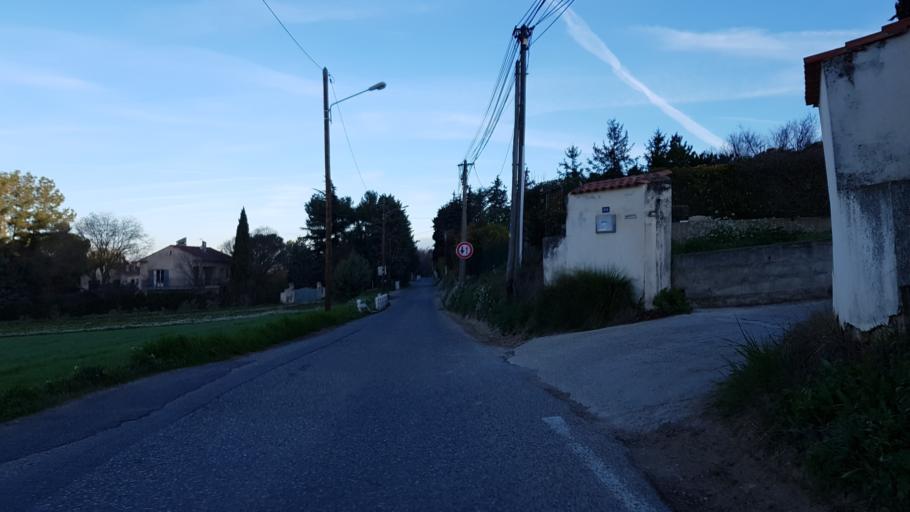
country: FR
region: Provence-Alpes-Cote d'Azur
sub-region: Departement des Bouches-du-Rhone
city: Bouc-Bel-Air
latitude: 43.4913
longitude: 5.4136
